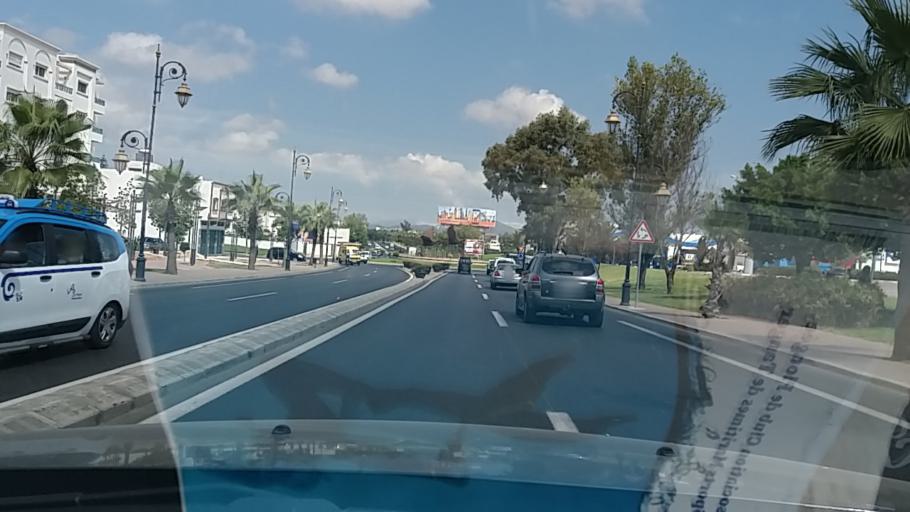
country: MA
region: Tanger-Tetouan
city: Tetouan
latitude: 35.6030
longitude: -5.3360
